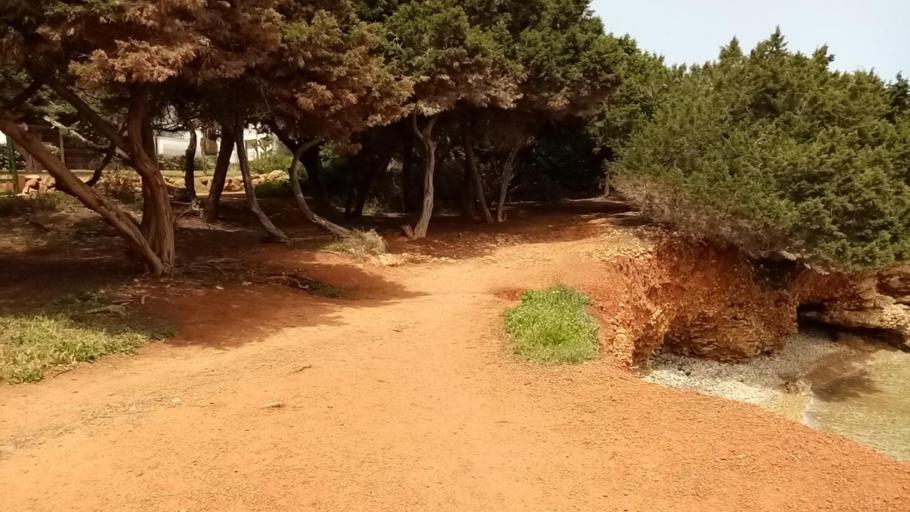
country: ES
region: Balearic Islands
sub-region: Illes Balears
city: Santa Eularia des Riu
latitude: 38.9876
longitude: 1.5459
